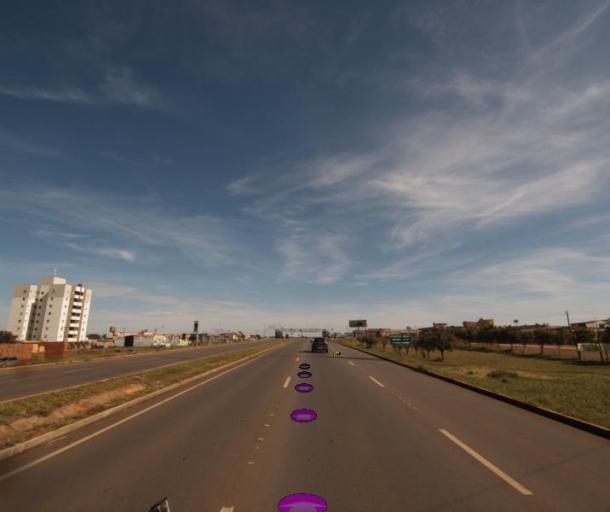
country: BR
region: Federal District
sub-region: Brasilia
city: Brasilia
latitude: -15.7533
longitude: -48.2585
